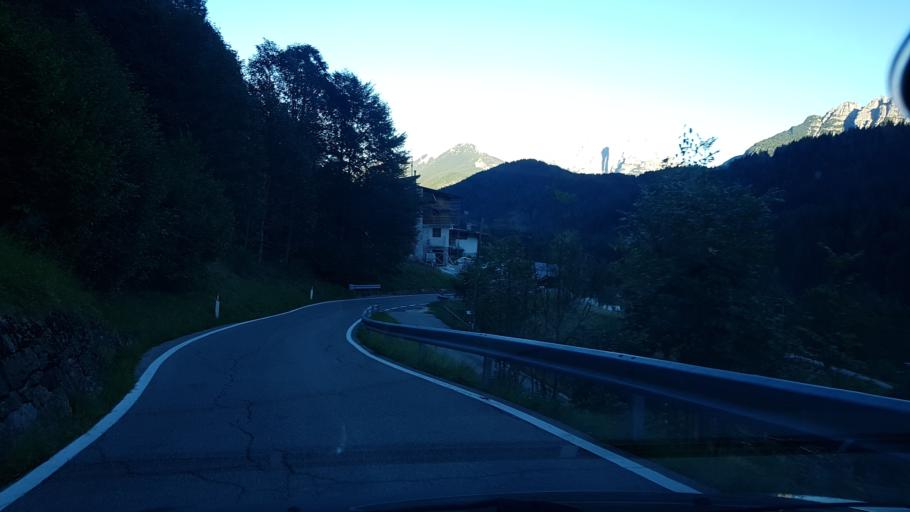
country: IT
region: Veneto
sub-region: Provincia di Belluno
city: Fusine
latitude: 46.3446
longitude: 12.1124
